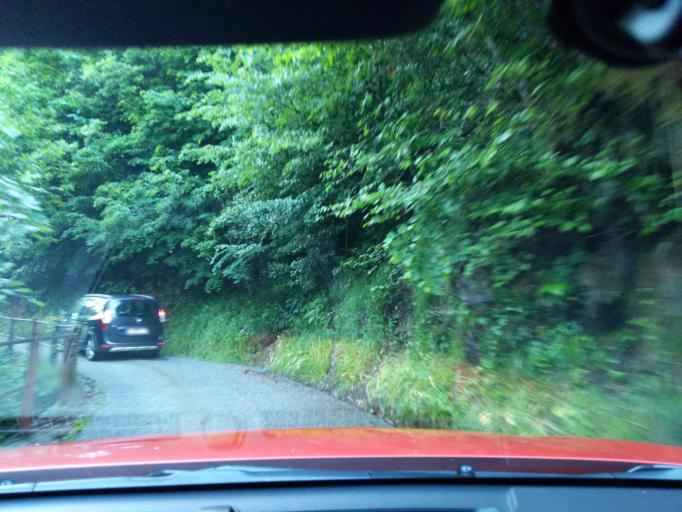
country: IT
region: Piedmont
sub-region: Provincia Verbano-Cusio-Ossola
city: Falmenta
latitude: 46.0899
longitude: 8.5967
